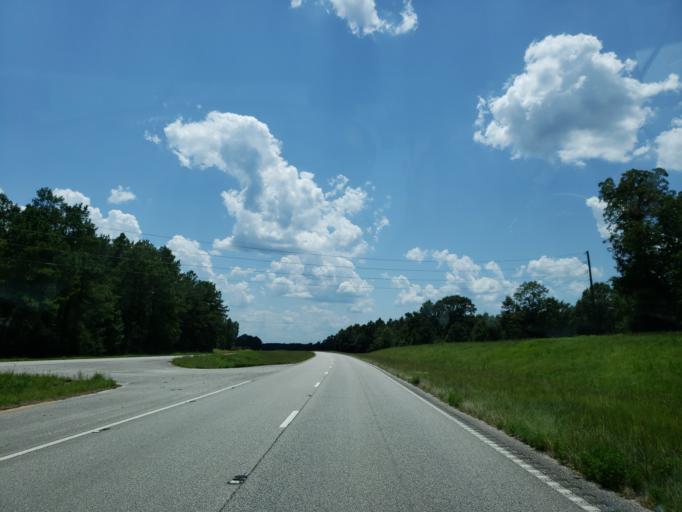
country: US
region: Mississippi
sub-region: Wayne County
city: Belmont
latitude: 31.3608
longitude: -88.4978
